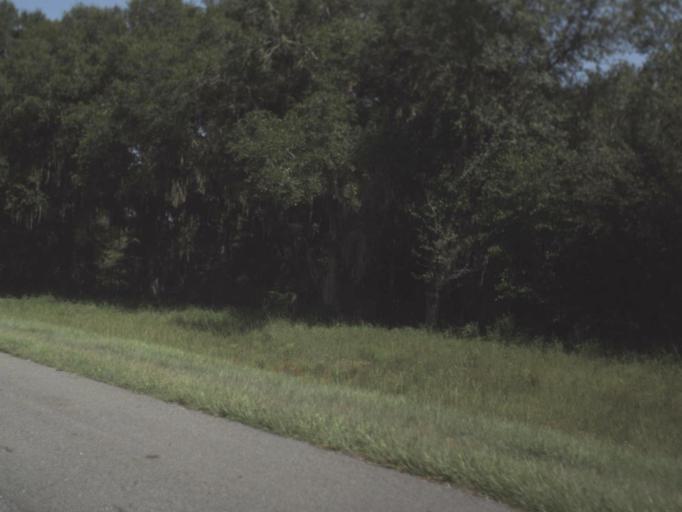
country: US
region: Florida
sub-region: Suwannee County
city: Live Oak
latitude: 30.3530
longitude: -83.0425
